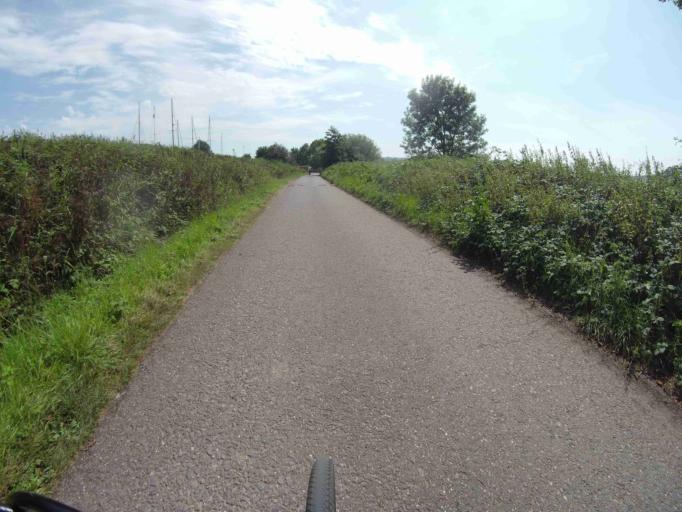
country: GB
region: England
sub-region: Devon
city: Topsham
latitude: 50.6658
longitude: -3.4684
